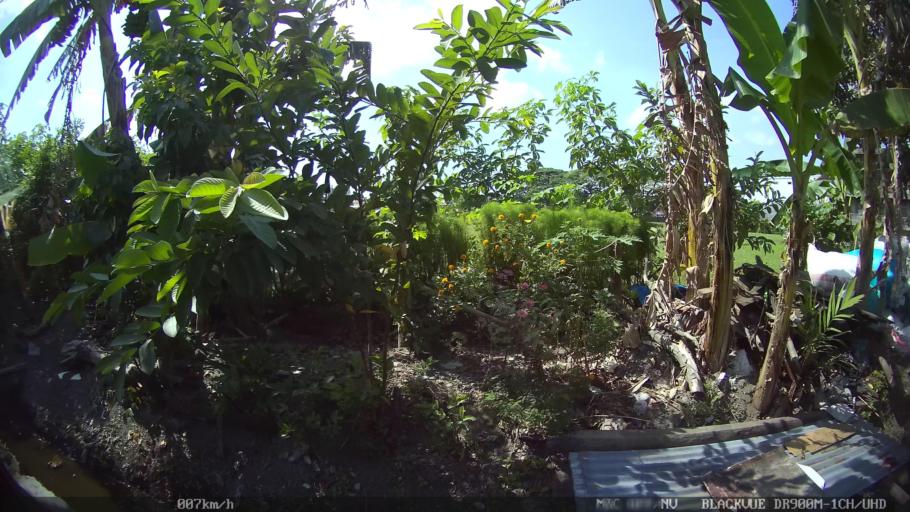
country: ID
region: Daerah Istimewa Yogyakarta
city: Kasihan
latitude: -7.8352
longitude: 110.3701
